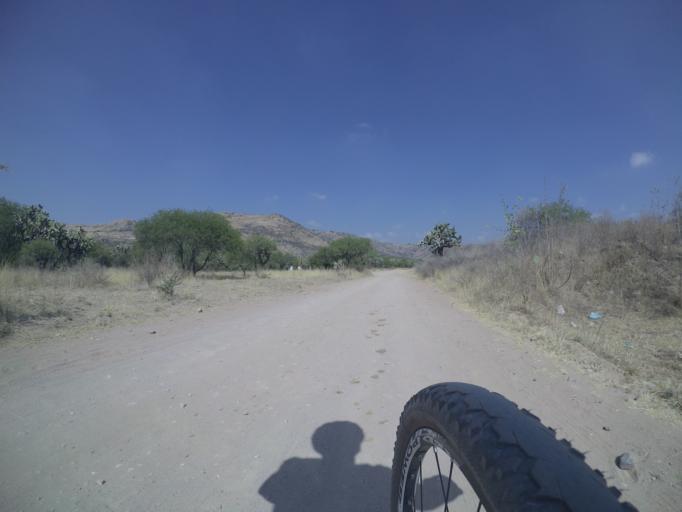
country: MX
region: Aguascalientes
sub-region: Jesus Maria
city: Paseos de las Haciendas [Fraccionamiento]
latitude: 22.0012
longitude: -102.3659
